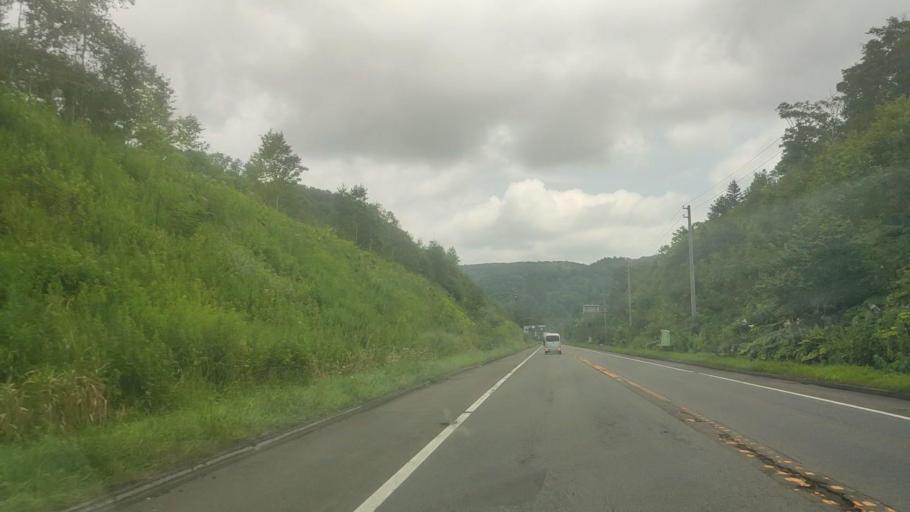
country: JP
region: Hokkaido
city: Niseko Town
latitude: 42.5934
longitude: 140.5287
